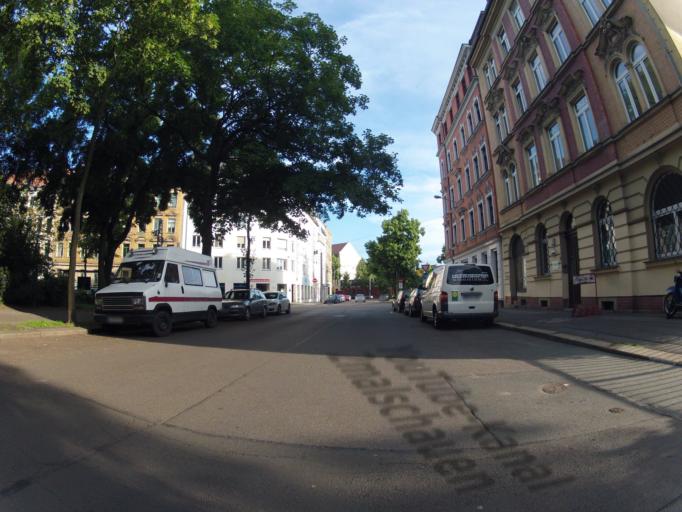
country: DE
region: Saxony
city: Leipzig
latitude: 51.3097
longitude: 12.3763
